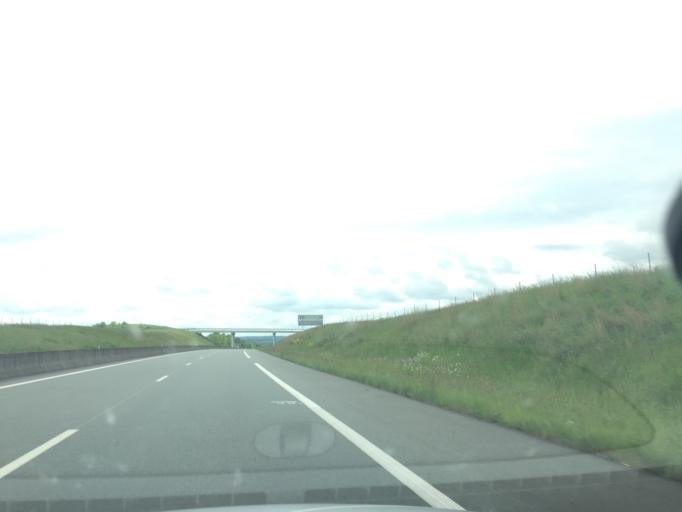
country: FR
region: Pays de la Loire
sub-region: Departement de la Sarthe
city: Luceau
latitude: 47.6843
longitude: 0.3676
